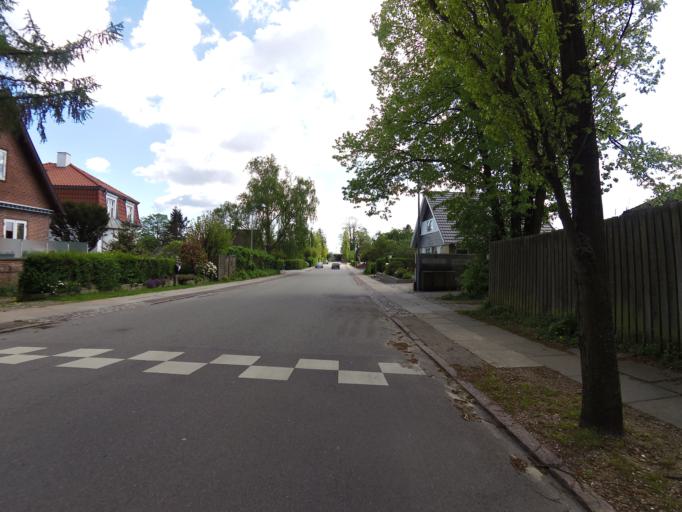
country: DK
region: Capital Region
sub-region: Gladsaxe Municipality
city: Buddinge
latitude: 55.7327
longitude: 12.5074
